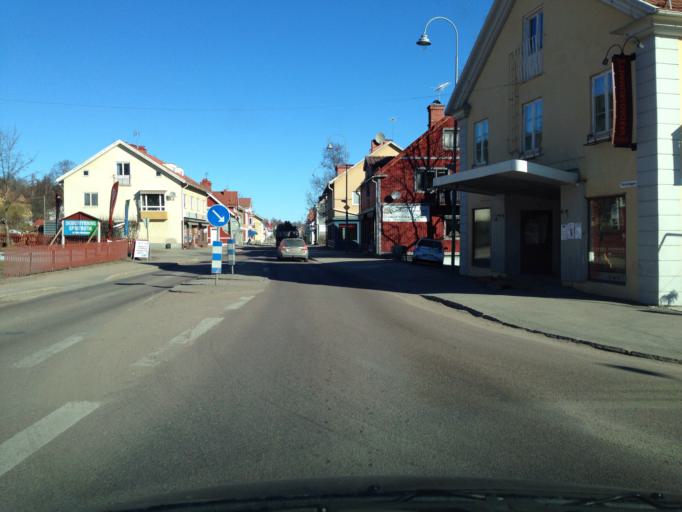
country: SE
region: Gaevleborg
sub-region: Ljusdals Kommun
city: Jaervsoe
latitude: 61.7134
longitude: 16.1690
